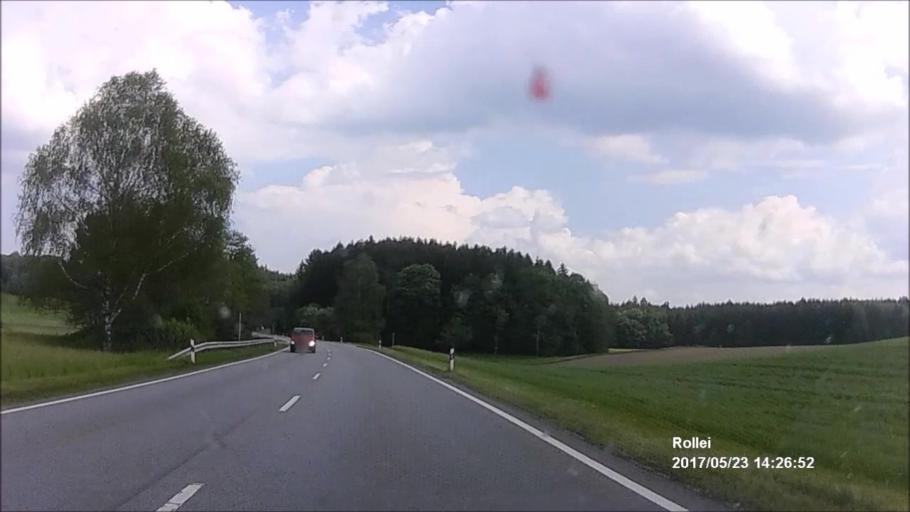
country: DE
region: Bavaria
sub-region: Upper Bavaria
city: Schnaitsee
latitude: 48.0337
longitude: 12.3441
